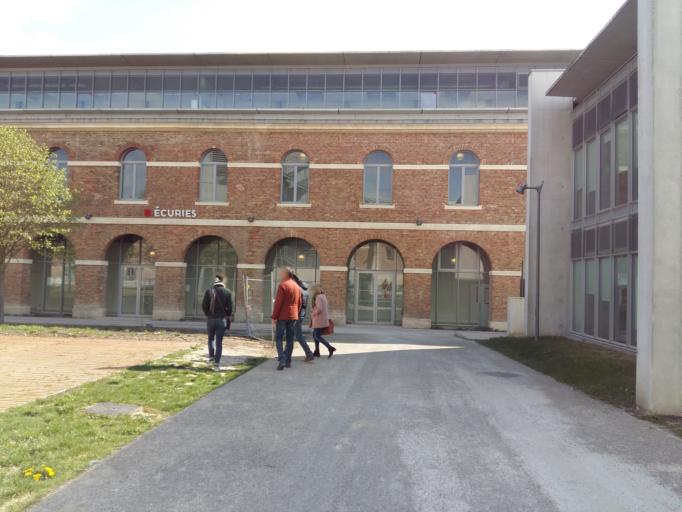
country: FR
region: Picardie
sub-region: Departement de la Somme
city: Amiens
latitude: 49.9041
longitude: 2.2980
